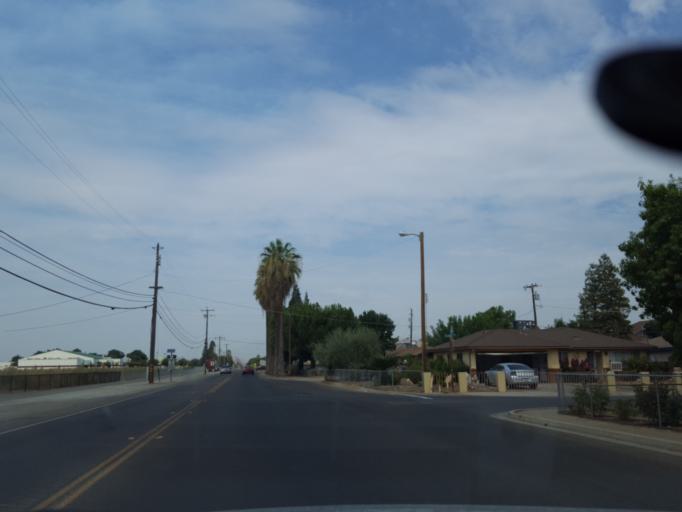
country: US
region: California
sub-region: Tulare County
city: Orosi
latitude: 36.5501
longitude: -119.2870
